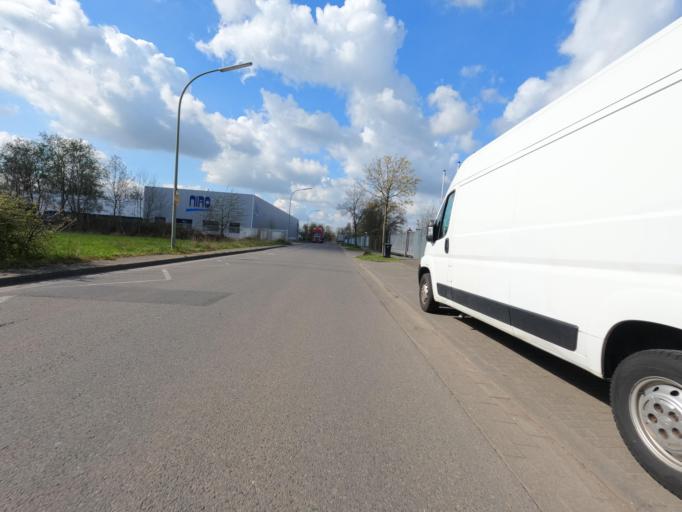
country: DE
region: North Rhine-Westphalia
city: Huckelhoven
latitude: 51.0322
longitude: 6.2661
